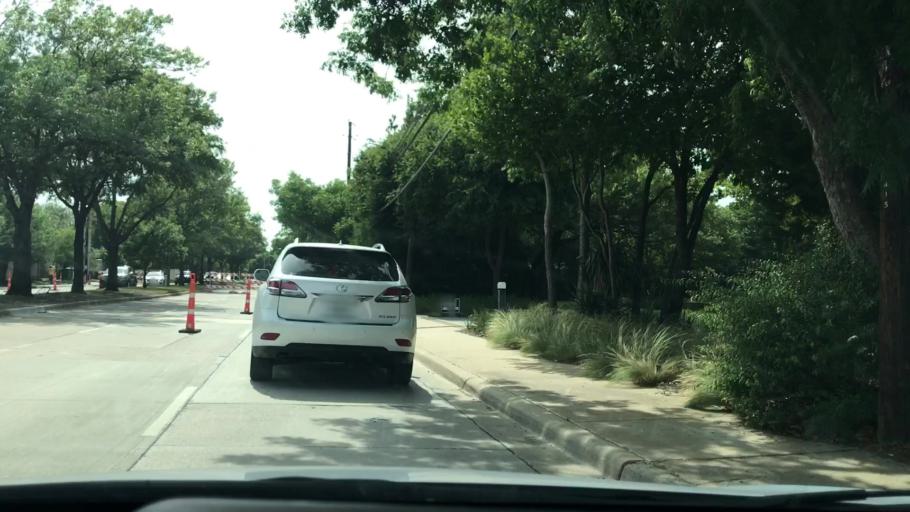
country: US
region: Texas
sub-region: Dallas County
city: University Park
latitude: 32.8802
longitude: -96.8146
